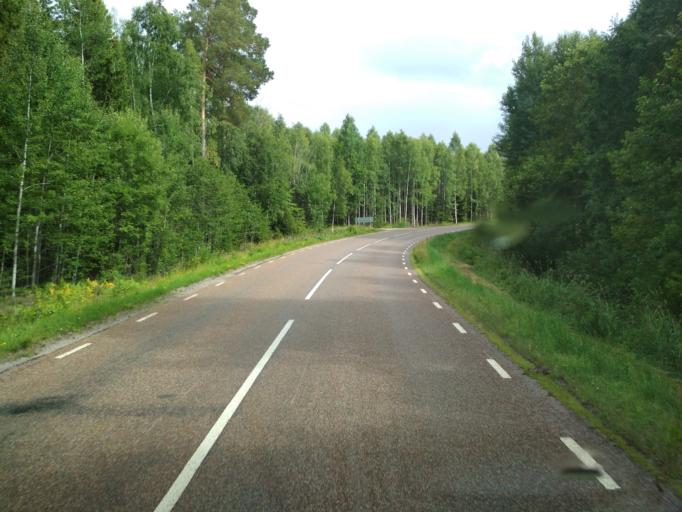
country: SE
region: Vaestmanland
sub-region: Norbergs Kommun
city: Norberg
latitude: 59.9532
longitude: 16.0177
